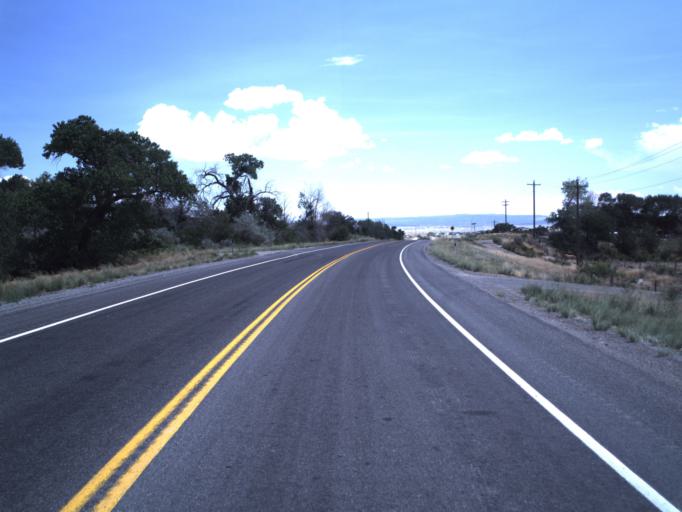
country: US
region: Utah
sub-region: Emery County
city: Huntington
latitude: 39.3512
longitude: -111.0023
